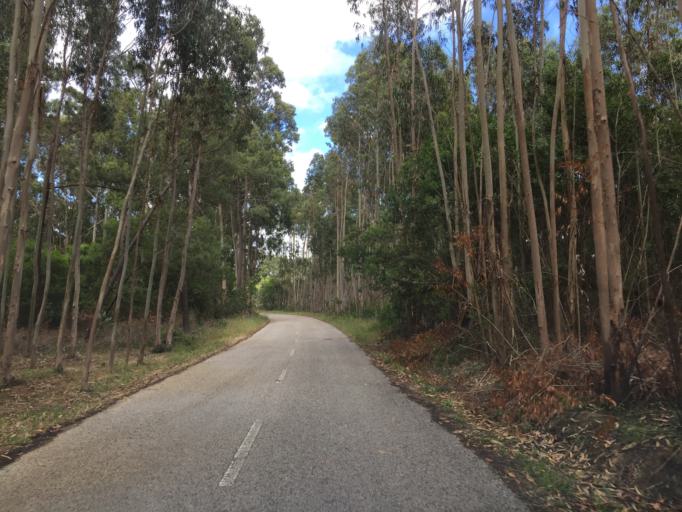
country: PT
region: Coimbra
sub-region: Figueira da Foz
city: Tavarede
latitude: 40.2108
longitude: -8.8390
